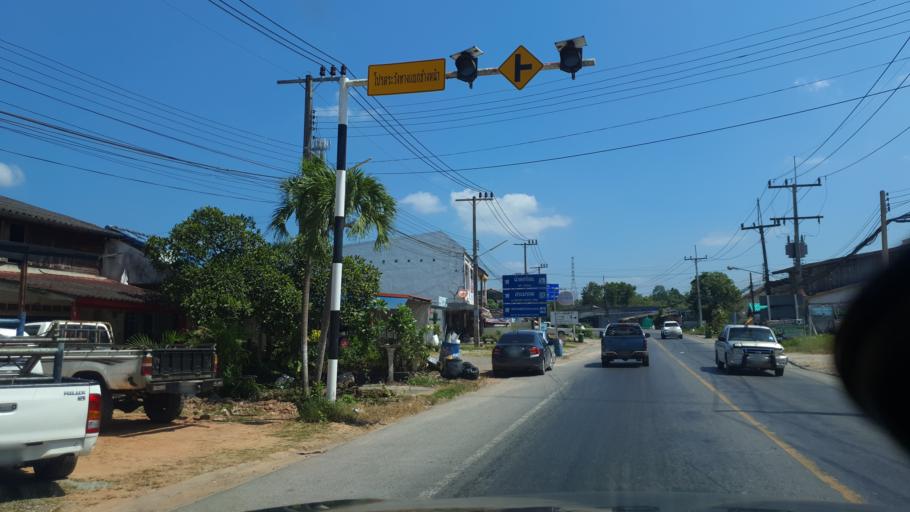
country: TH
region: Krabi
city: Khlong Thom
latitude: 7.9381
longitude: 99.1451
